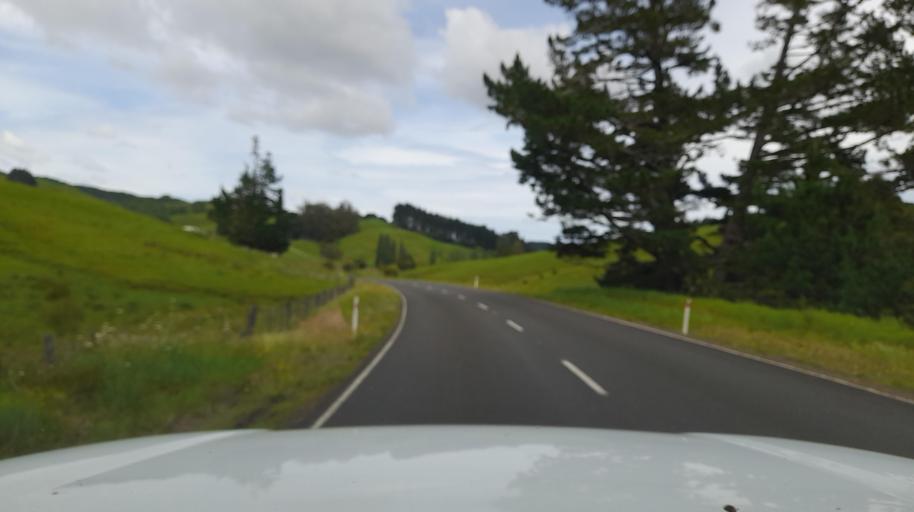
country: NZ
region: Northland
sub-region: Far North District
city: Kaitaia
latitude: -35.2661
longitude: 173.2927
